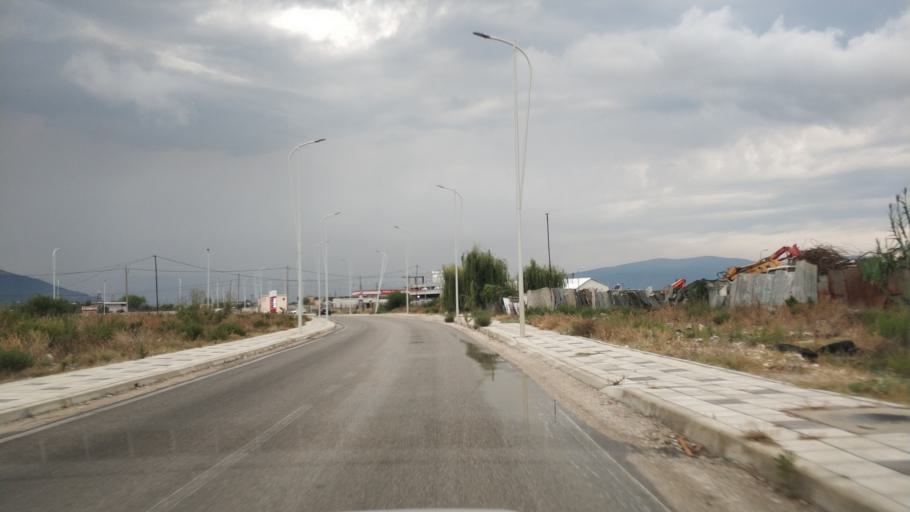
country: AL
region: Vlore
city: Vlore
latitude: 40.4829
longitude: 19.4668
